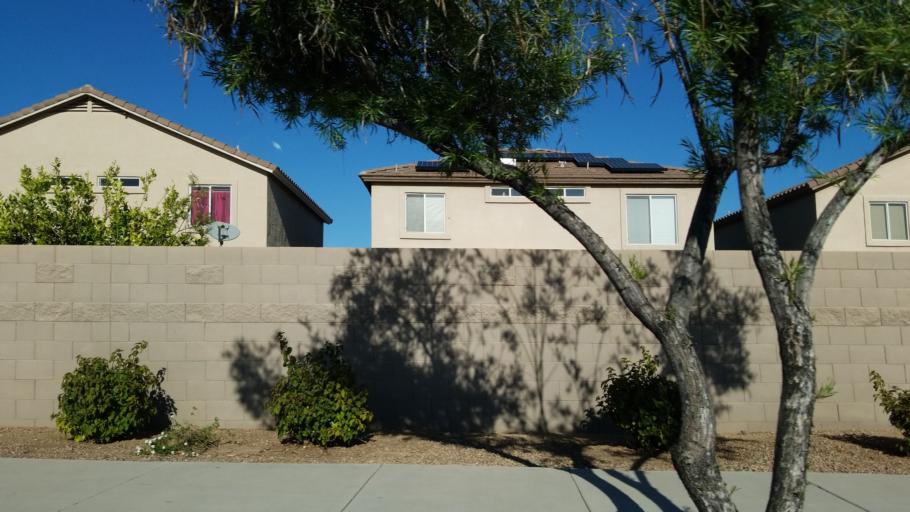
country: US
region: Arizona
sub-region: Maricopa County
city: Youngtown
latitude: 33.5768
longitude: -112.3113
